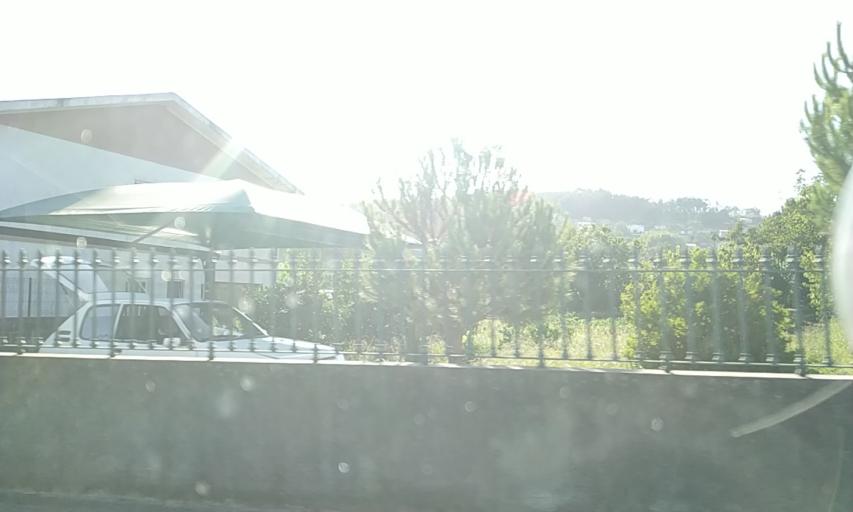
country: PT
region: Porto
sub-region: Santo Tirso
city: Sao Miguel do Couto
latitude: 41.2872
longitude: -8.4719
